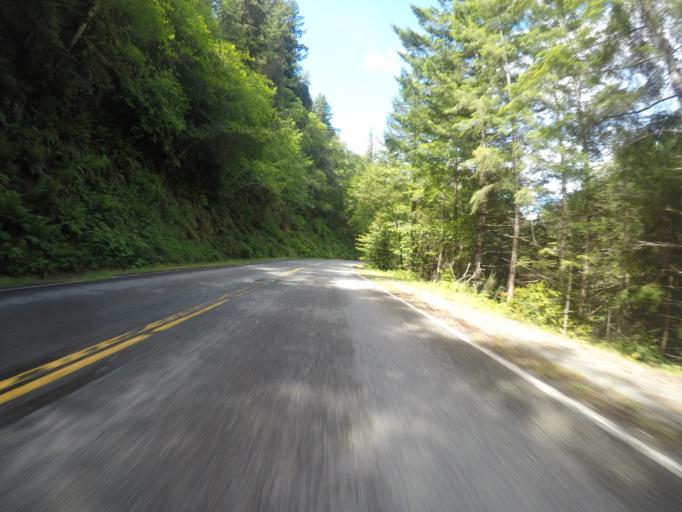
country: US
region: California
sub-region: Del Norte County
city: Bertsch-Oceanview
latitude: 41.7952
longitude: -124.0441
